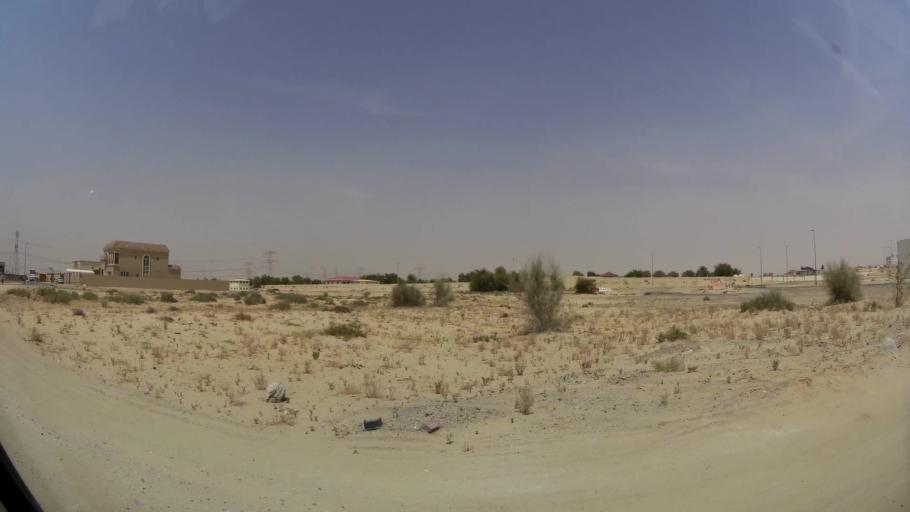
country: AE
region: Ash Shariqah
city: Sharjah
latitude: 25.2498
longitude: 55.5086
